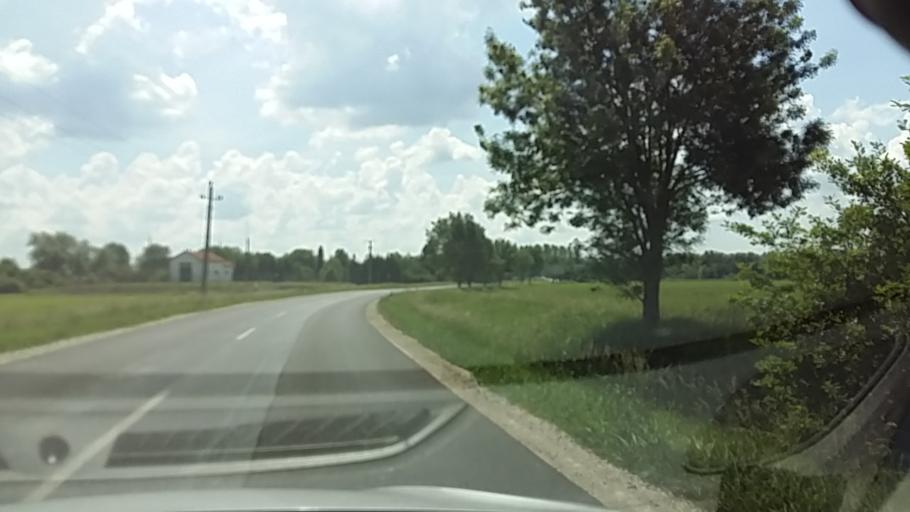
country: AT
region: Burgenland
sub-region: Politischer Bezirk Gussing
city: Moschendorf
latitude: 46.9664
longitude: 16.5092
